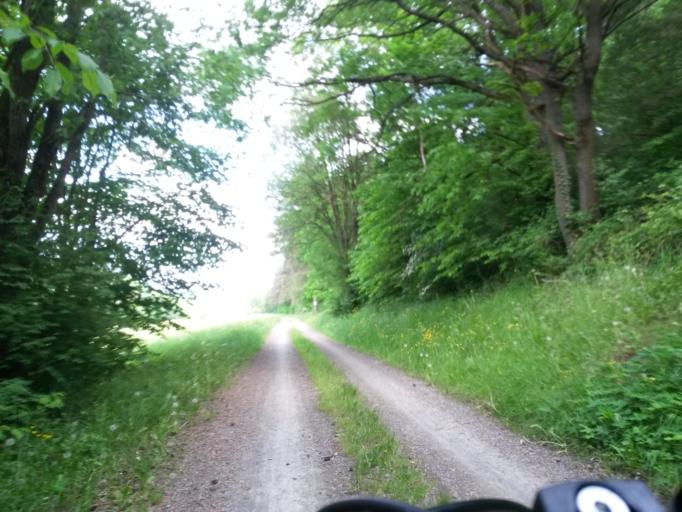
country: DE
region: Bavaria
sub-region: Regierungsbezirk Unterfranken
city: Euerdorf
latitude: 50.1543
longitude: 10.0342
